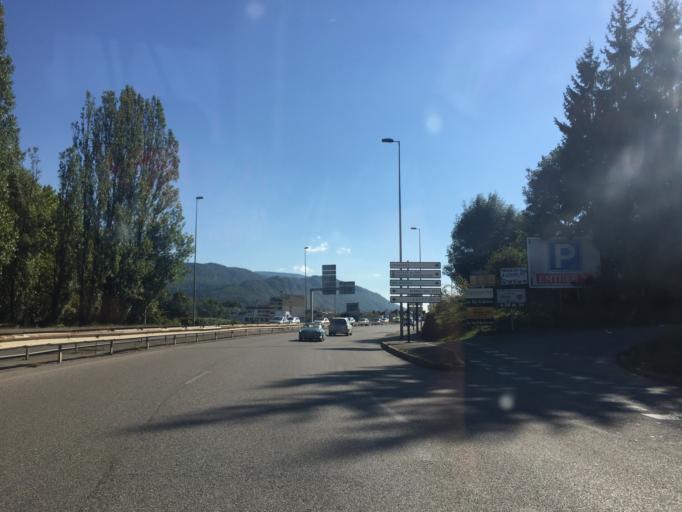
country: FR
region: Rhone-Alpes
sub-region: Departement de la Haute-Savoie
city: Annecy
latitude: 45.8939
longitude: 6.1113
